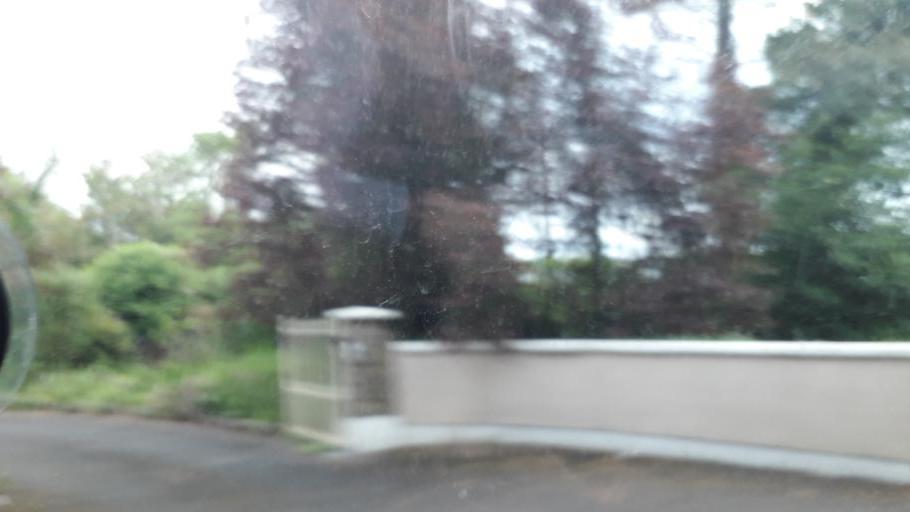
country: IE
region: Leinster
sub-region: Kildare
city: Celbridge
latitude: 53.3179
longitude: -6.5495
